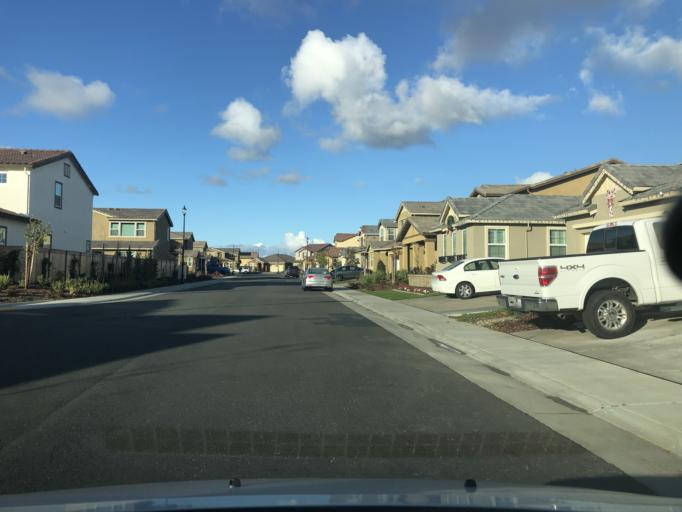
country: US
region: California
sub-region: Sacramento County
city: Antelope
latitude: 38.7702
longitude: -121.3775
